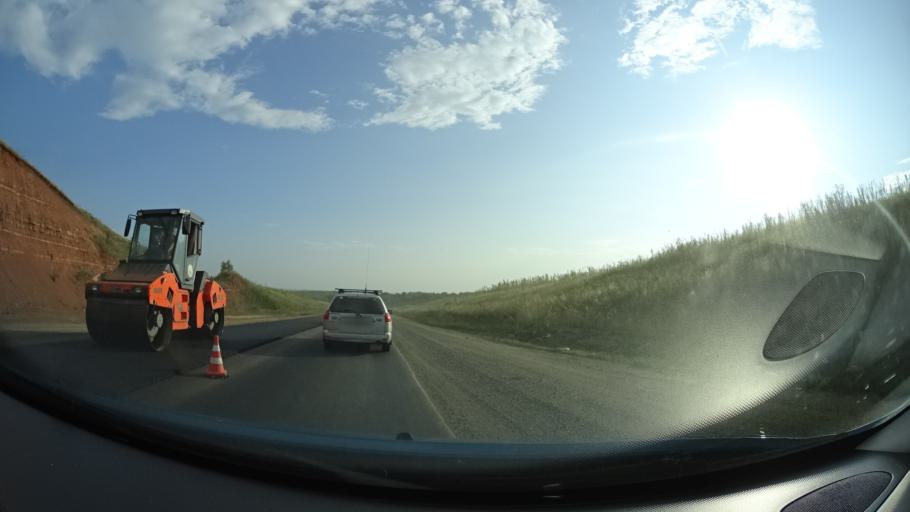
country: RU
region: Orenburg
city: Severnoye
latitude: 54.1727
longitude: 52.6475
